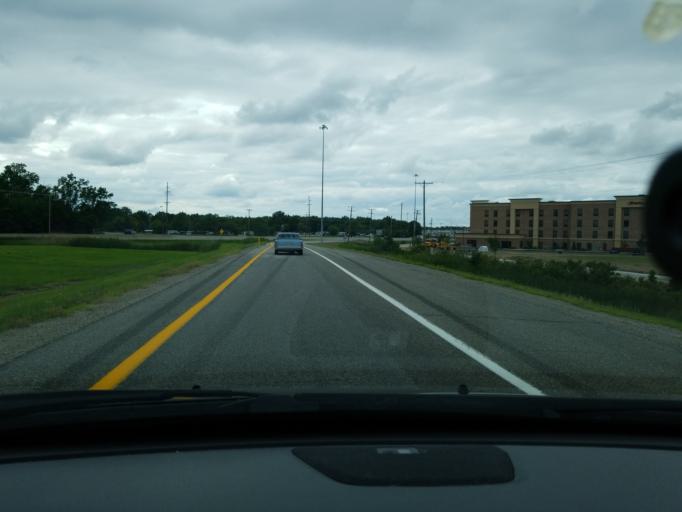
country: US
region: Ohio
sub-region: Lorain County
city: Elyria
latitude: 41.3913
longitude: -82.1149
